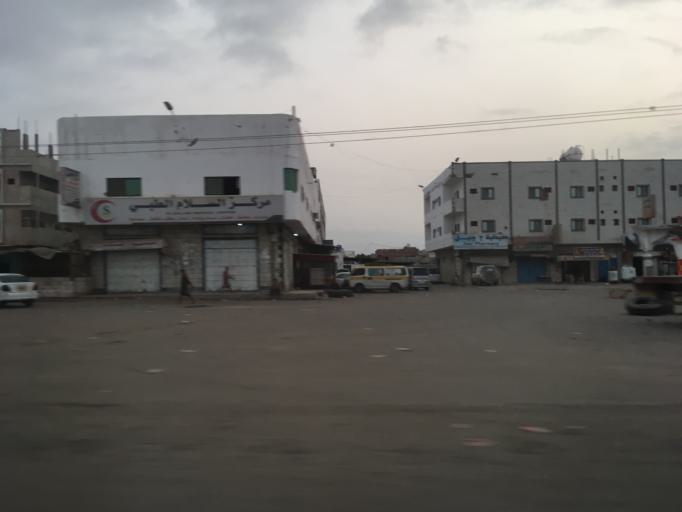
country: YE
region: Lahij
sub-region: Al  Hawtah
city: Lahij
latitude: 13.0068
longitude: 44.9098
